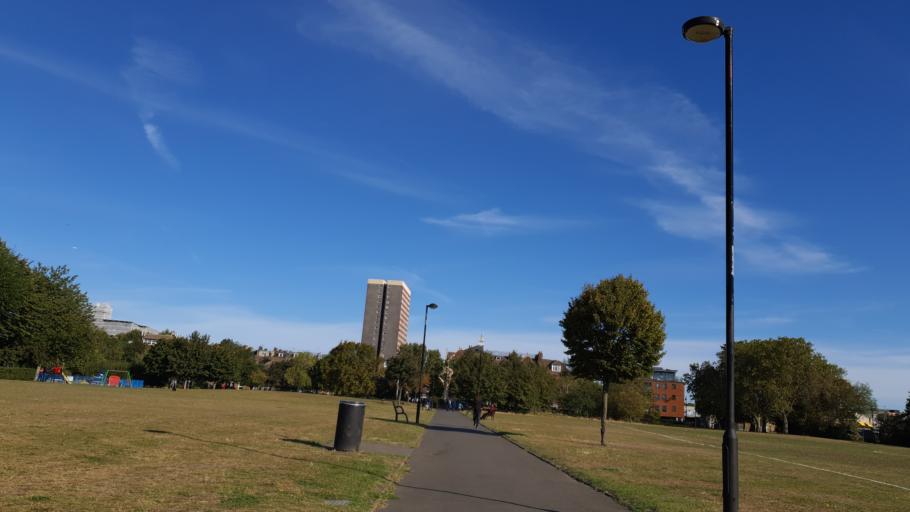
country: GB
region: England
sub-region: Greater London
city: Bethnal Green
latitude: 51.5247
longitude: -0.0610
